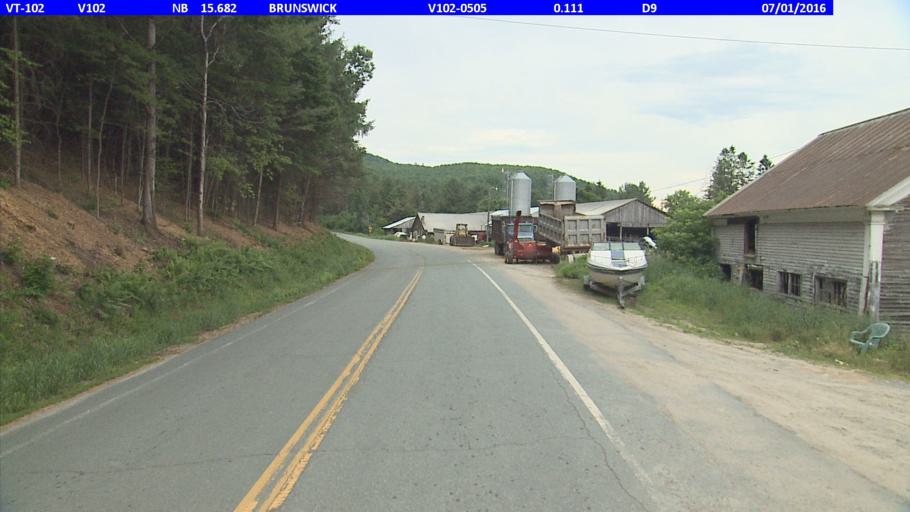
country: US
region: New Hampshire
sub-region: Coos County
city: Stratford
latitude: 44.6642
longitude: -71.5913
